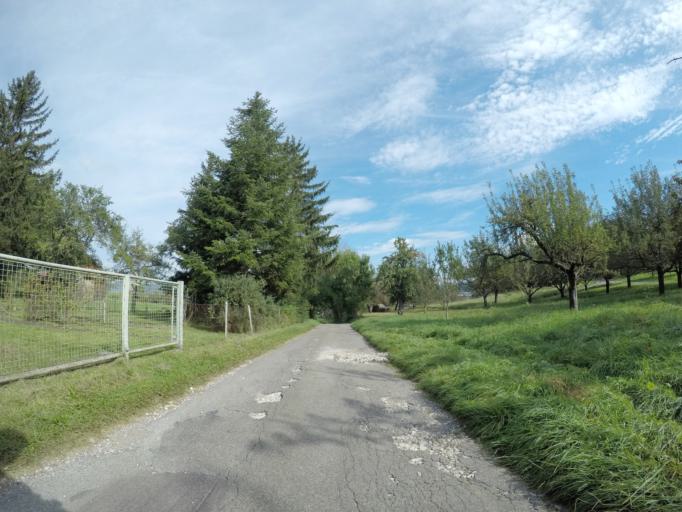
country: DE
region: Baden-Wuerttemberg
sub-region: Tuebingen Region
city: Pfullingen
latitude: 48.4583
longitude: 9.2038
